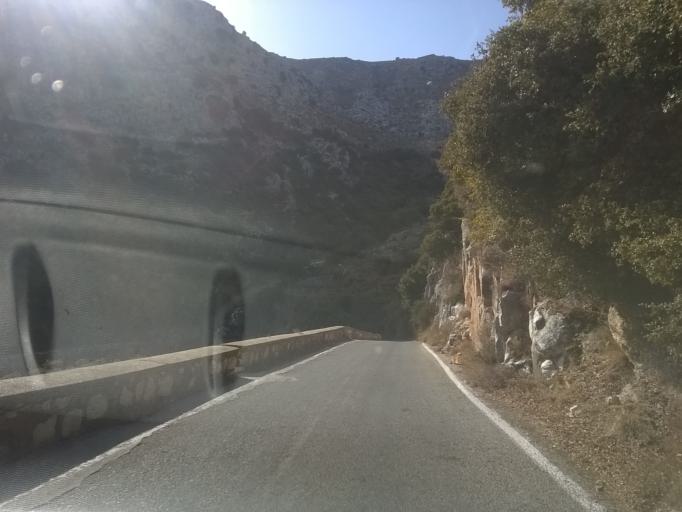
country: GR
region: South Aegean
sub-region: Nomos Kykladon
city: Filotion
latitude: 37.1243
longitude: 25.5315
